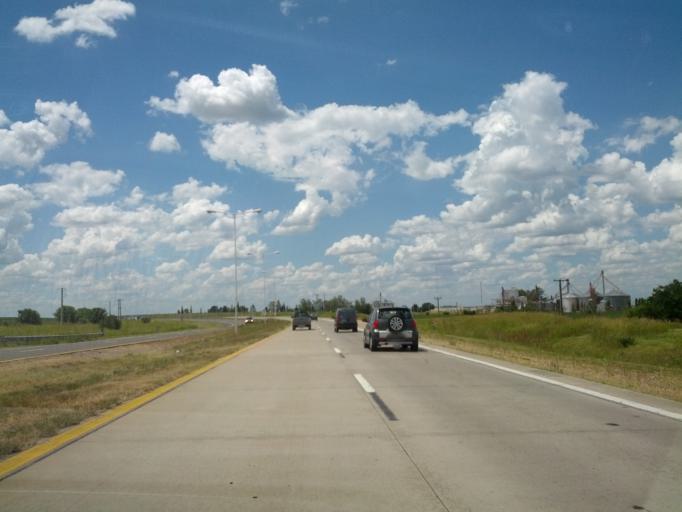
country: AR
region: Entre Rios
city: Gualeguaychu
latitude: -32.9049
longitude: -58.5554
